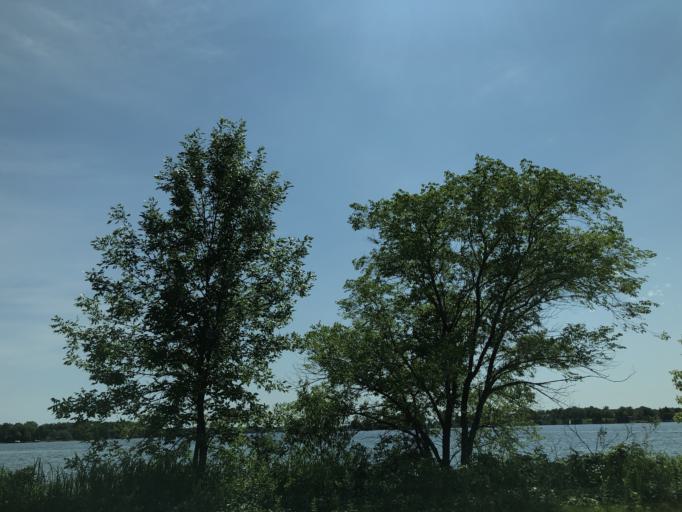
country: US
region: Minnesota
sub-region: Douglas County
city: Alexandria
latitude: 45.9320
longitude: -95.3797
